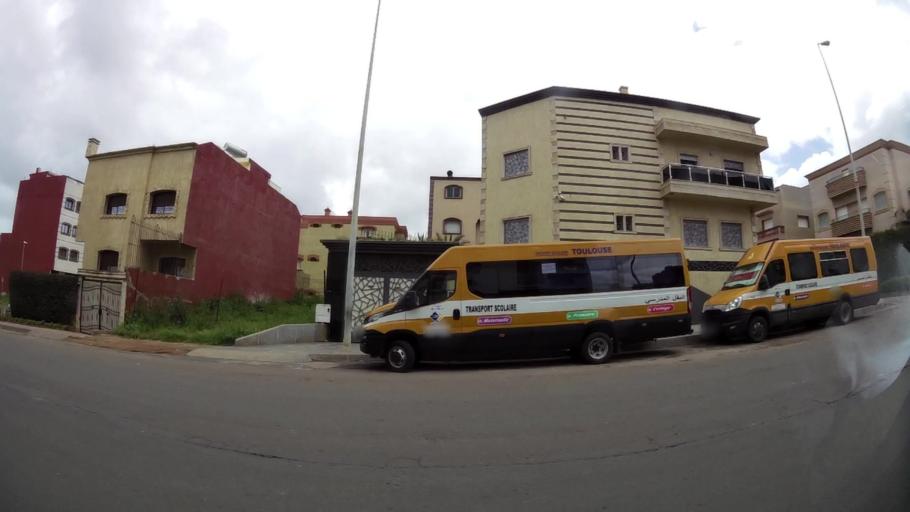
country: MA
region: Grand Casablanca
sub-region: Casablanca
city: Casablanca
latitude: 33.5324
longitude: -7.5882
